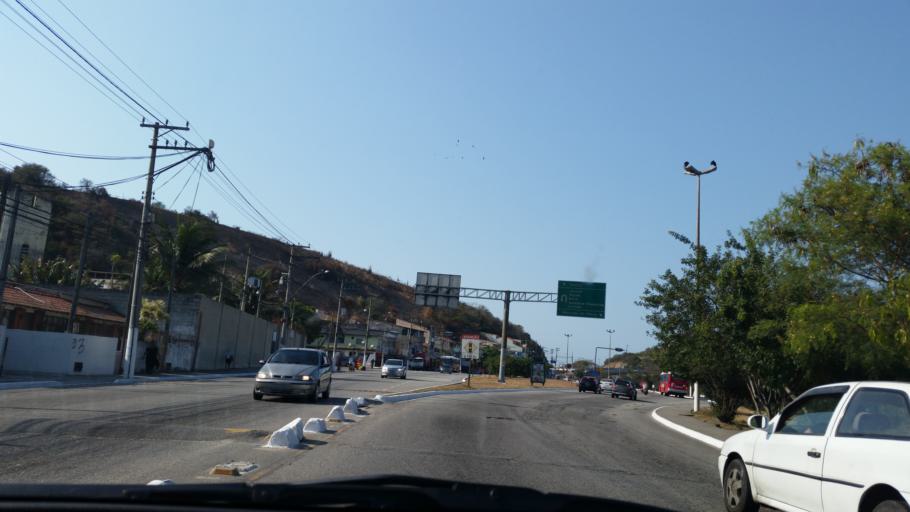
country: BR
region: Rio de Janeiro
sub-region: Cabo Frio
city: Cabo Frio
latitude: -22.8734
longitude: -42.0230
